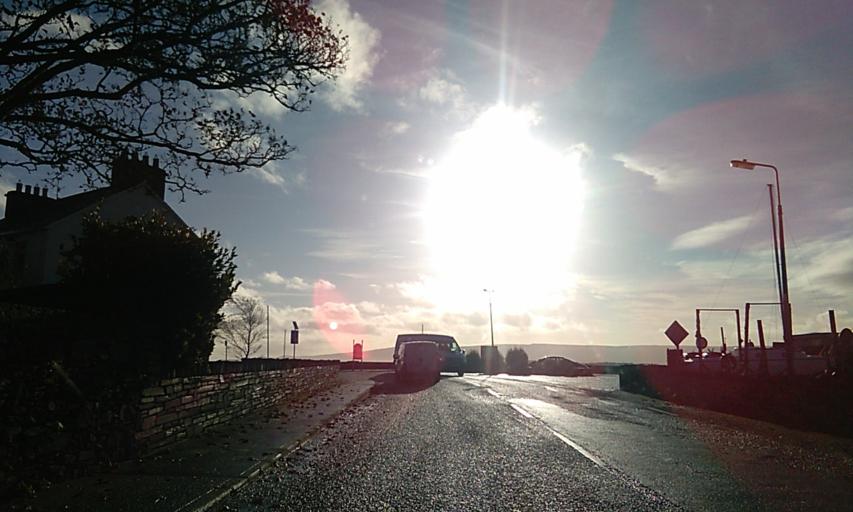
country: IE
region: Ulster
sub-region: County Donegal
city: Moville
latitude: 55.2035
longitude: -6.9820
